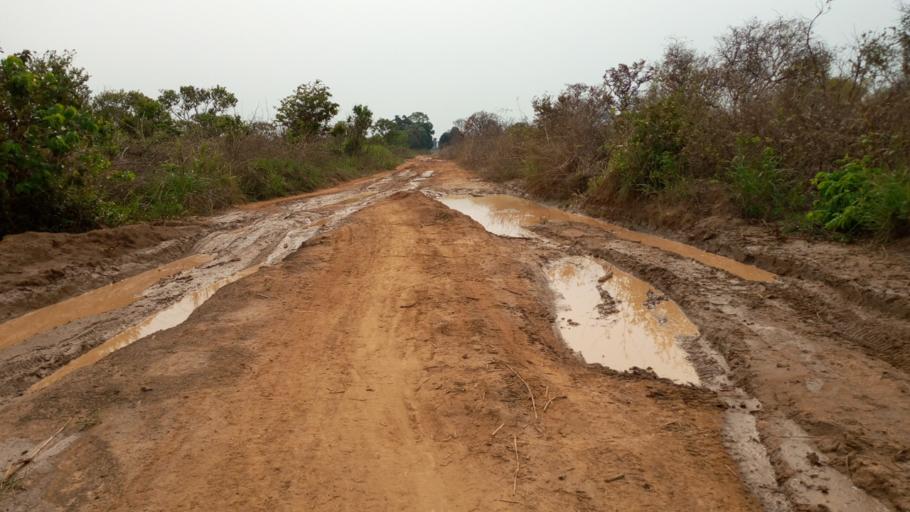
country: CD
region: Bandundu
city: Bandundu
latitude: -3.4521
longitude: 17.7559
